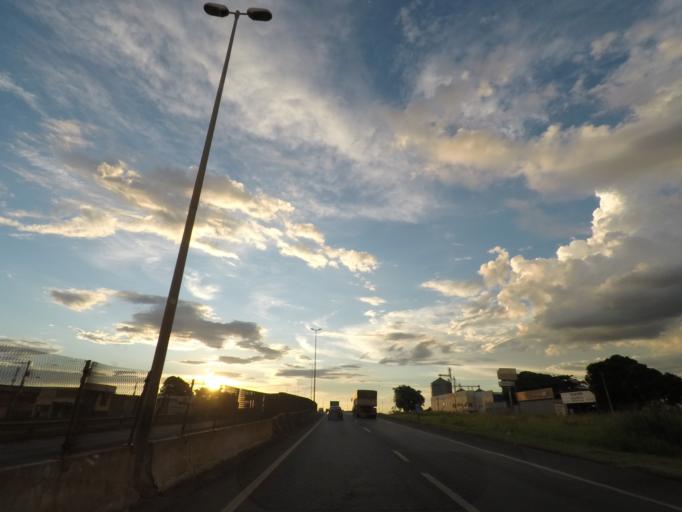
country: BR
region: Minas Gerais
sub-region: Uberaba
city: Uberaba
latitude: -19.7790
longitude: -47.9409
